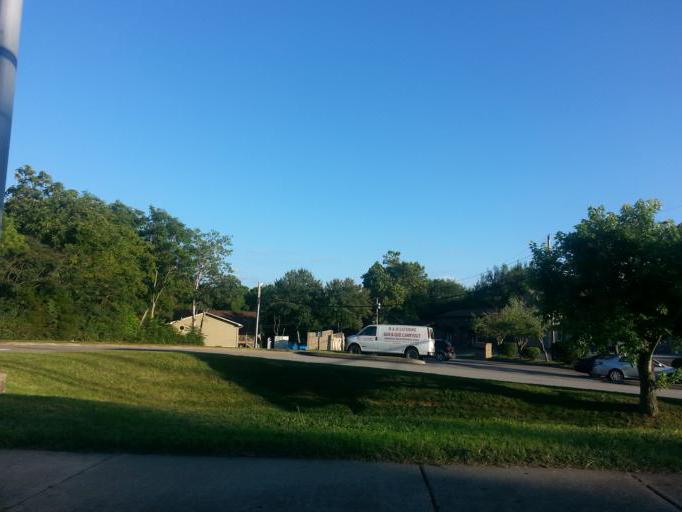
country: US
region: Tennessee
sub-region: Knox County
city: Farragut
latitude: 35.9431
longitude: -84.0852
